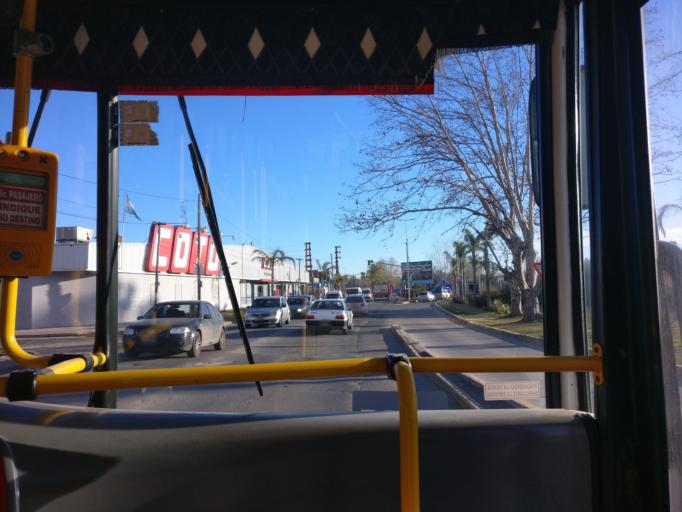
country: AR
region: Buenos Aires
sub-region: Partido de Ezeiza
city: Ezeiza
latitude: -34.8928
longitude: -58.5715
